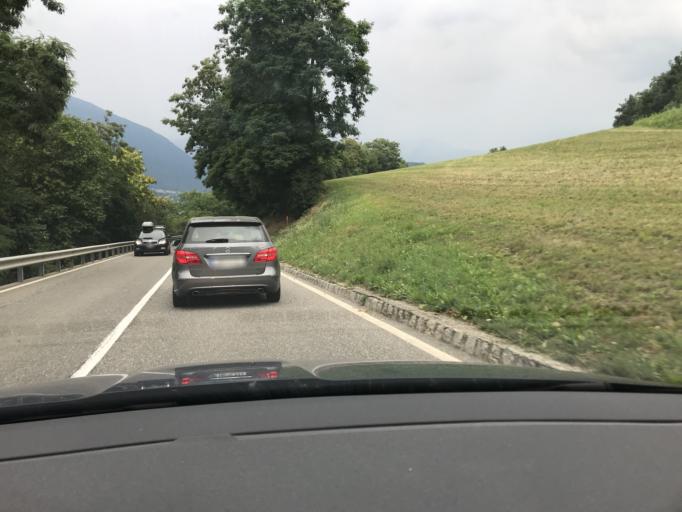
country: IT
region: Trentino-Alto Adige
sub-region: Bolzano
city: Bressanone
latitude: 46.6959
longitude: 11.6595
